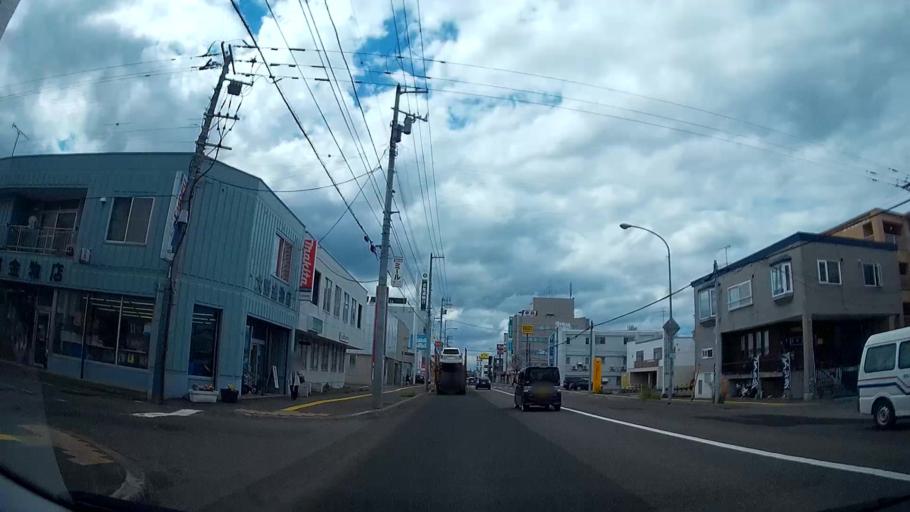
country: JP
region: Hokkaido
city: Chitose
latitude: 42.8795
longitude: 141.5790
